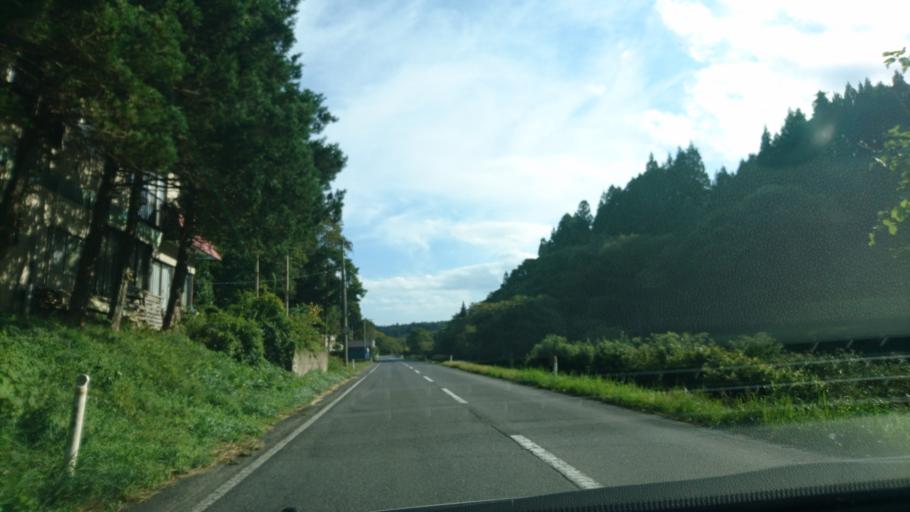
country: JP
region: Iwate
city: Ichinoseki
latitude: 38.8610
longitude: 141.3308
